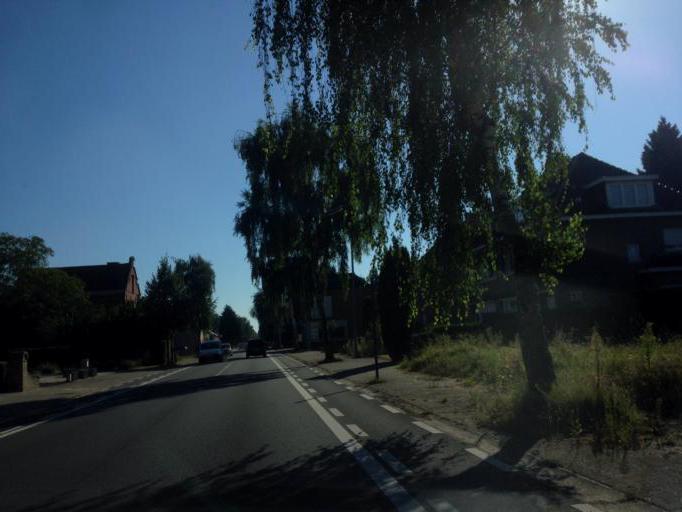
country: BE
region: Flanders
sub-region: Provincie Antwerpen
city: Geel
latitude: 51.1636
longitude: 5.0152
